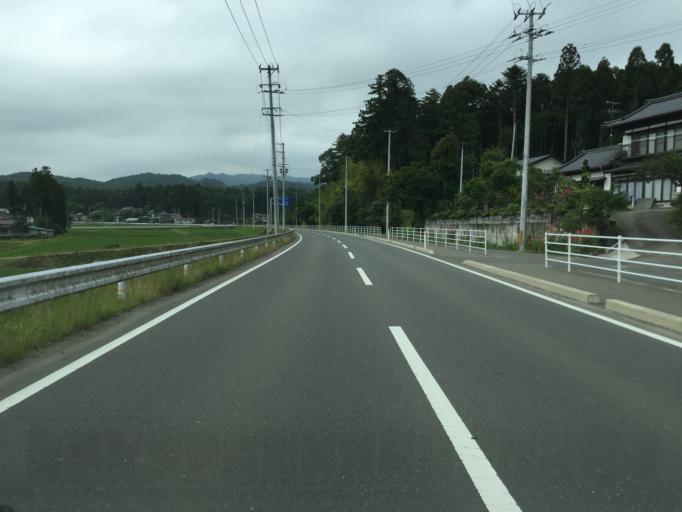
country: JP
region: Miyagi
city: Marumori
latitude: 37.7370
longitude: 140.9229
